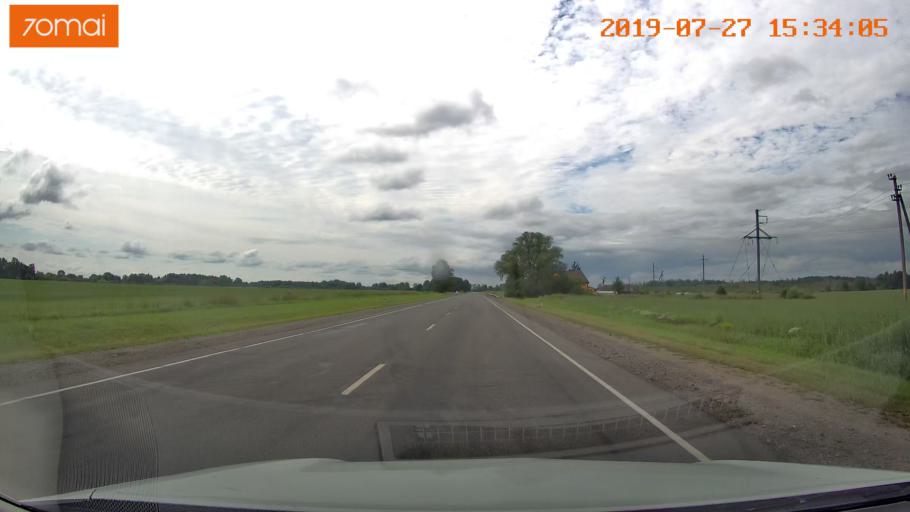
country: RU
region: Kaliningrad
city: Nesterov
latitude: 54.6120
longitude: 22.4337
